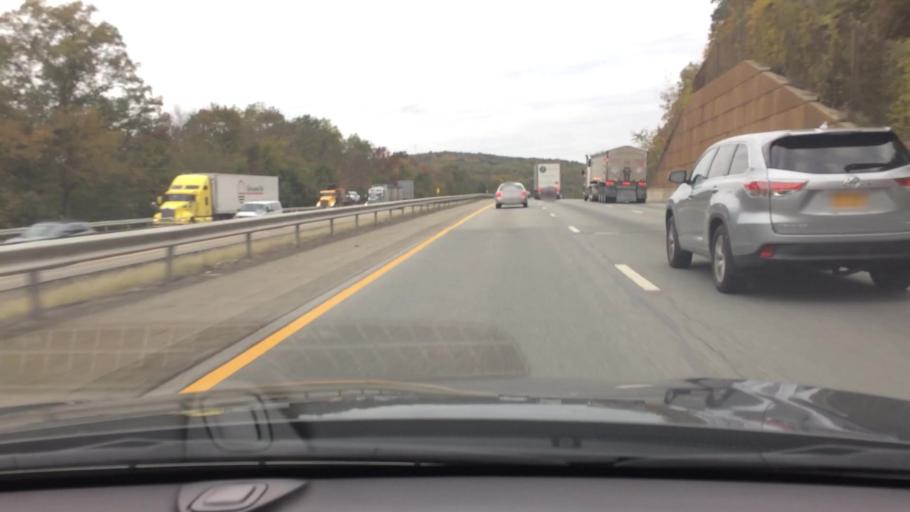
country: US
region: New York
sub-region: Rockland County
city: Sloatsburg
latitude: 41.1678
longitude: -74.1854
